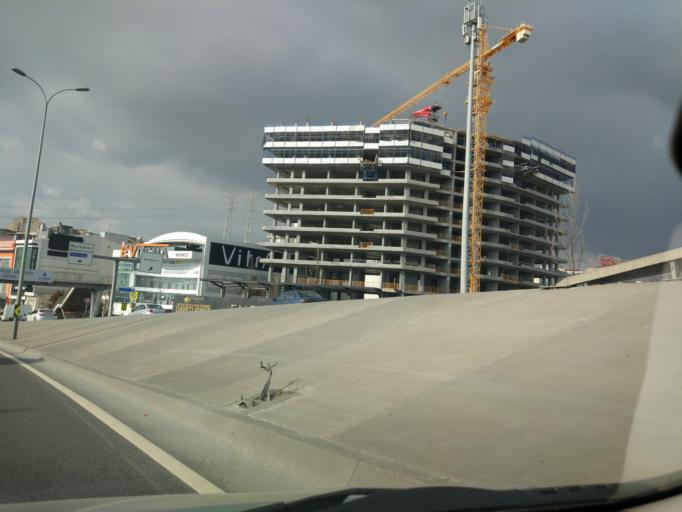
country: TR
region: Istanbul
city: Yakuplu
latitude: 40.9995
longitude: 28.6988
